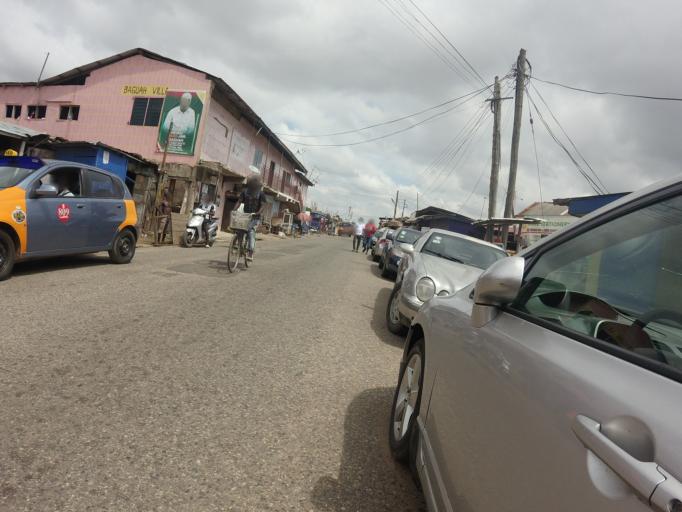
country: GH
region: Greater Accra
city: Accra
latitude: 5.5845
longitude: -0.2065
